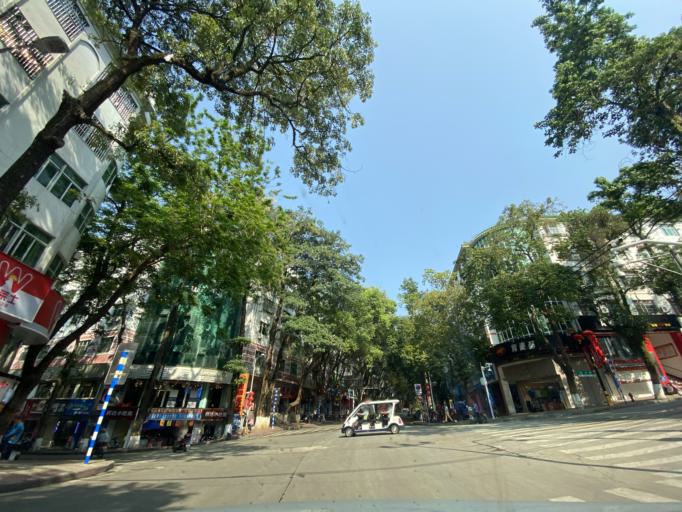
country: CN
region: Hainan
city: Chongshan
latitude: 18.7796
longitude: 109.5133
